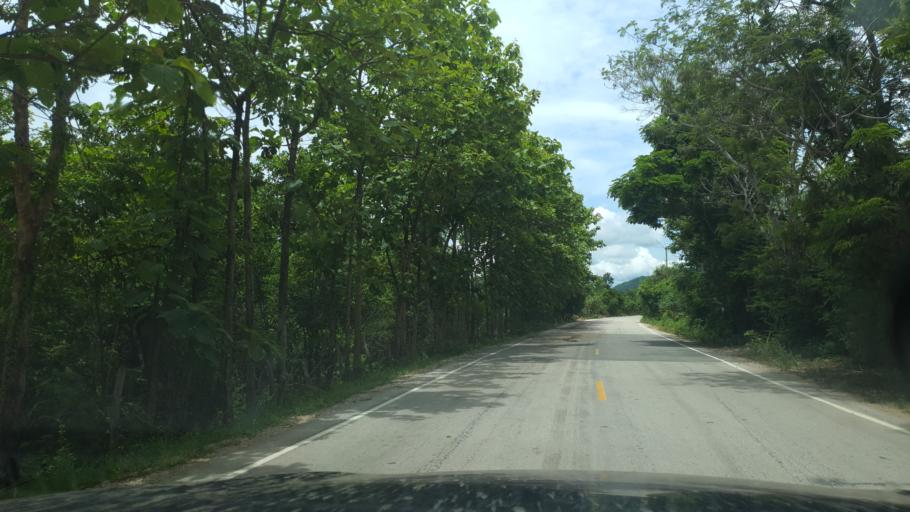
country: TH
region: Lampang
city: Sop Prap
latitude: 17.9199
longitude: 99.4046
